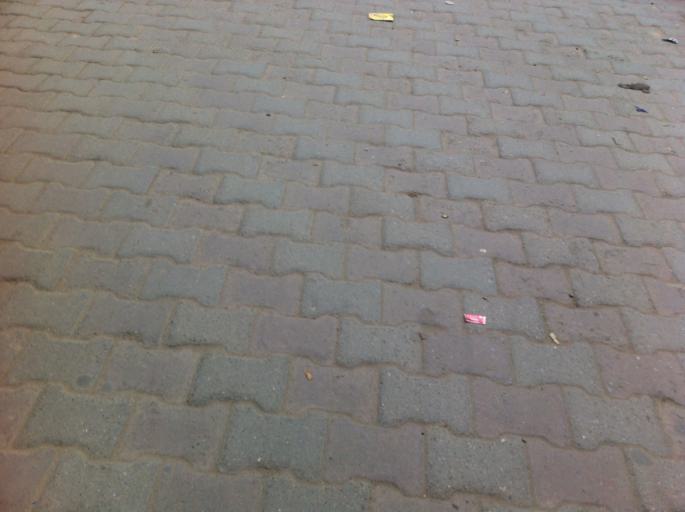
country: IN
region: Punjab
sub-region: Kapurthala
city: Phagwara
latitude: 31.2204
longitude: 75.7726
